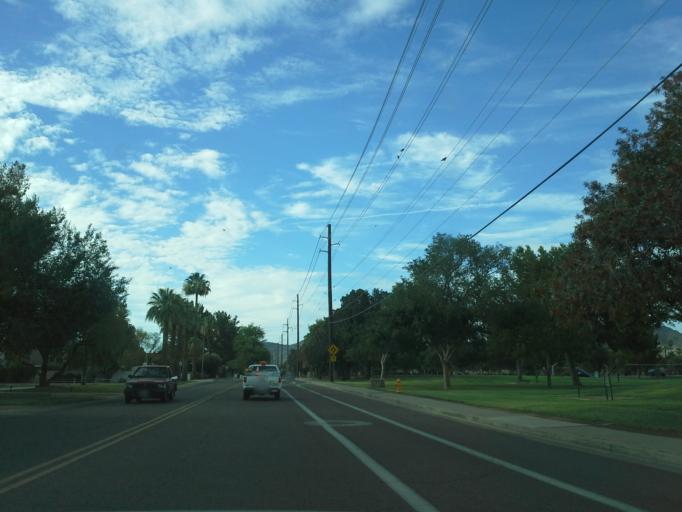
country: US
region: Arizona
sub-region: Maricopa County
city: Glendale
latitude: 33.5572
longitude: -112.0913
